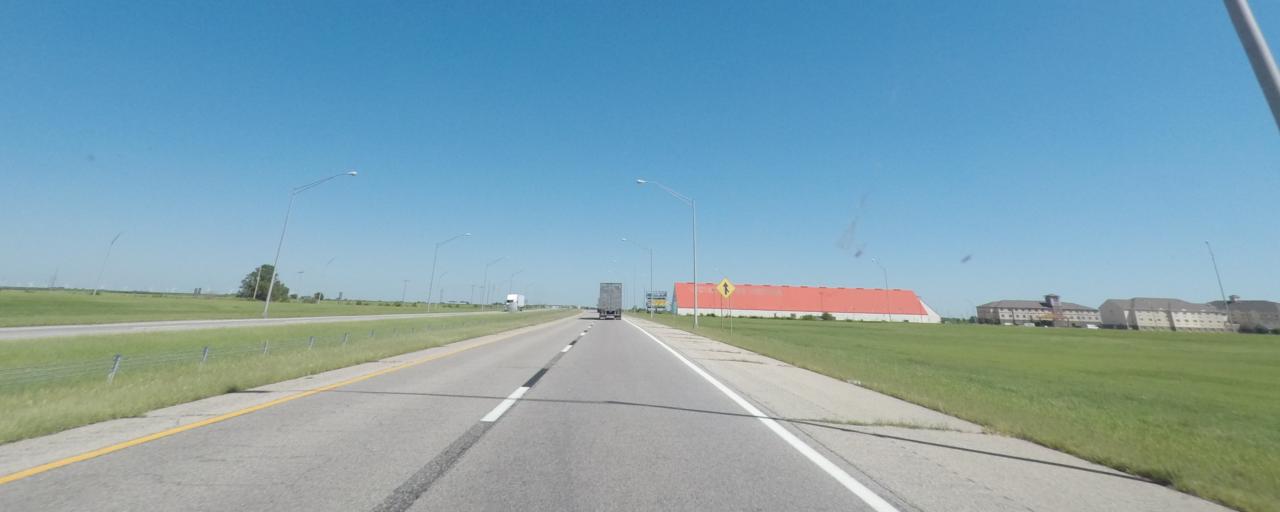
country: US
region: Oklahoma
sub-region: Kay County
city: Blackwell
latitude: 36.8121
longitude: -97.3423
